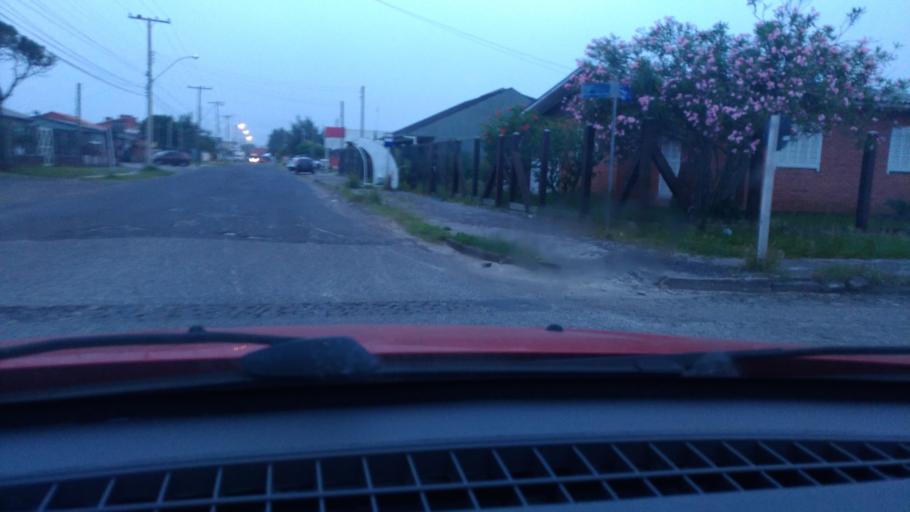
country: BR
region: Rio Grande do Sul
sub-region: Capao Da Canoa
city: Capao da Canoa
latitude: -29.8498
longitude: -50.0642
